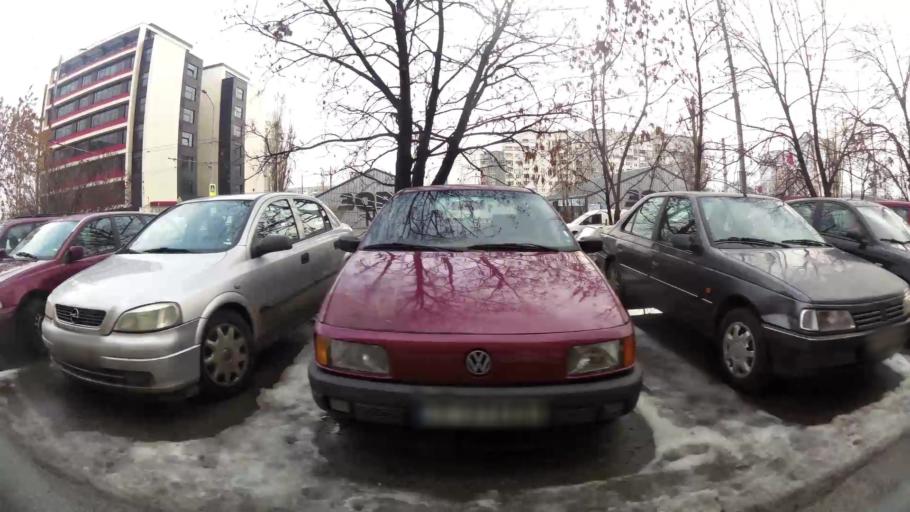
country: BG
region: Sofia-Capital
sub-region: Stolichna Obshtina
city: Sofia
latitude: 42.7149
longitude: 23.2619
